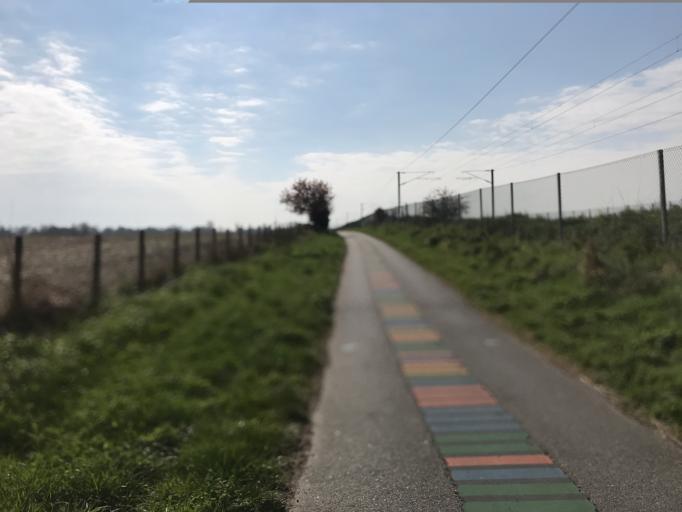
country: GB
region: England
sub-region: Cambridgeshire
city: Cambridge
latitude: 52.1651
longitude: 0.1326
